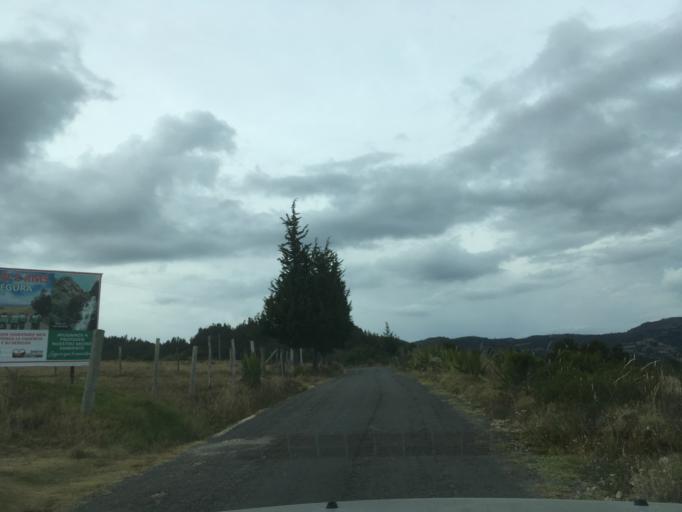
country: CO
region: Boyaca
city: Firavitoba
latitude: 5.6778
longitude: -73.0212
